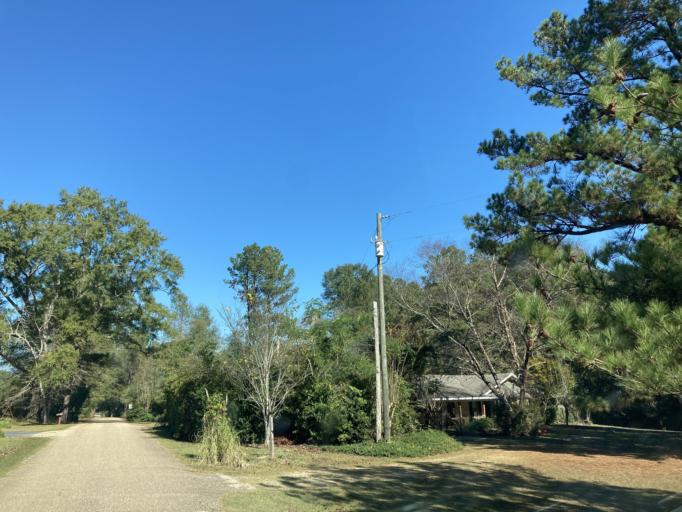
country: US
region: Mississippi
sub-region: Lamar County
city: West Hattiesburg
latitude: 31.3064
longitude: -89.4933
